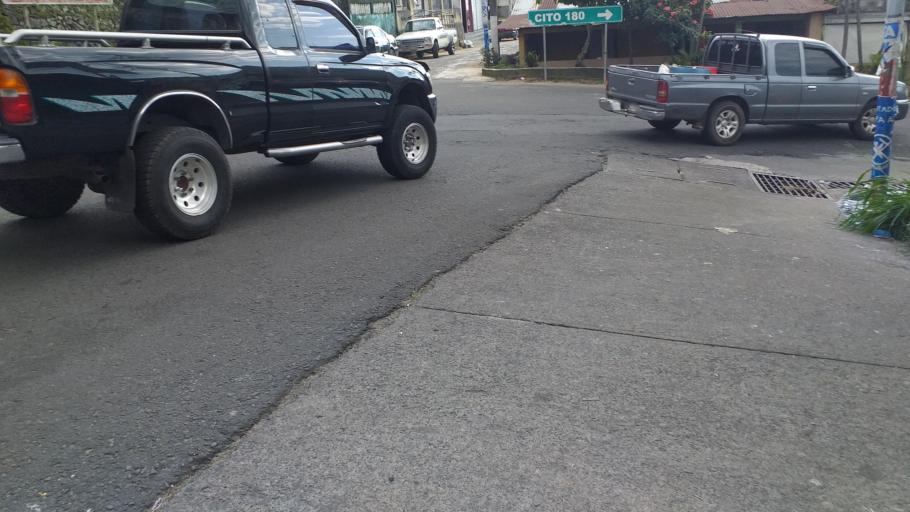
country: GT
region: Suchitepeque
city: Pueblo Nuevo
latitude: 14.6442
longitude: -91.5571
